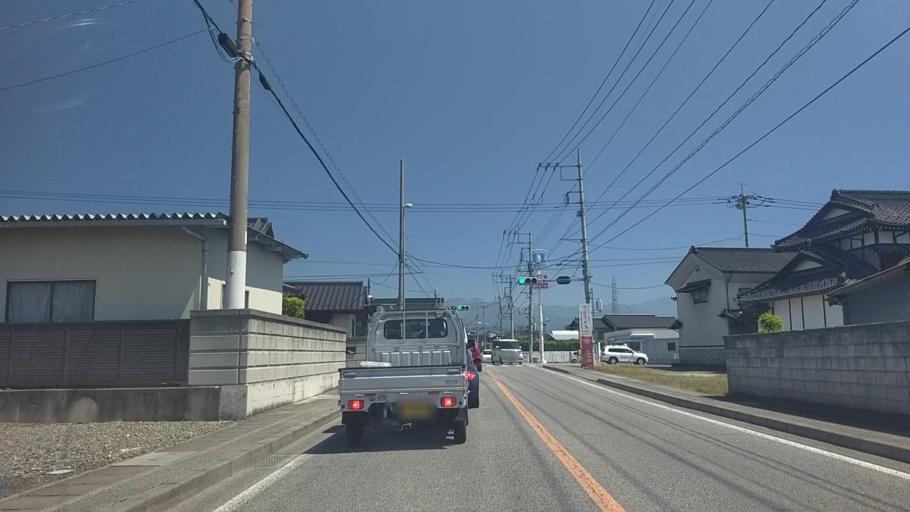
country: JP
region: Yamanashi
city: Ryuo
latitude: 35.6554
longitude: 138.4642
